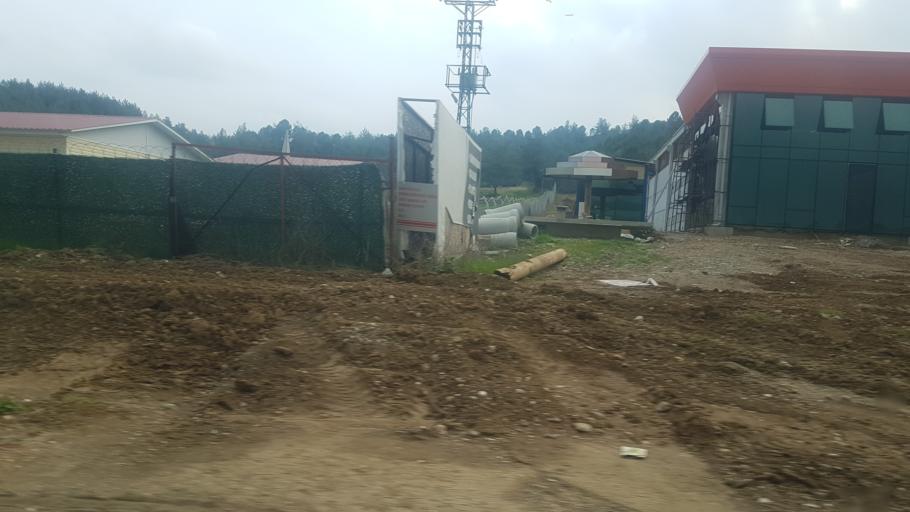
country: TR
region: Mersin
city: Yenice
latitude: 37.0918
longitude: 35.1483
